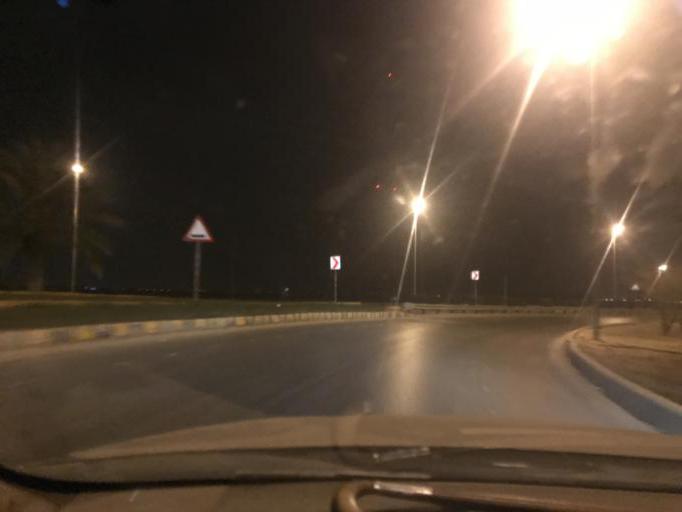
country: SA
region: Ar Riyad
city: Riyadh
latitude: 24.8252
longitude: 46.7166
